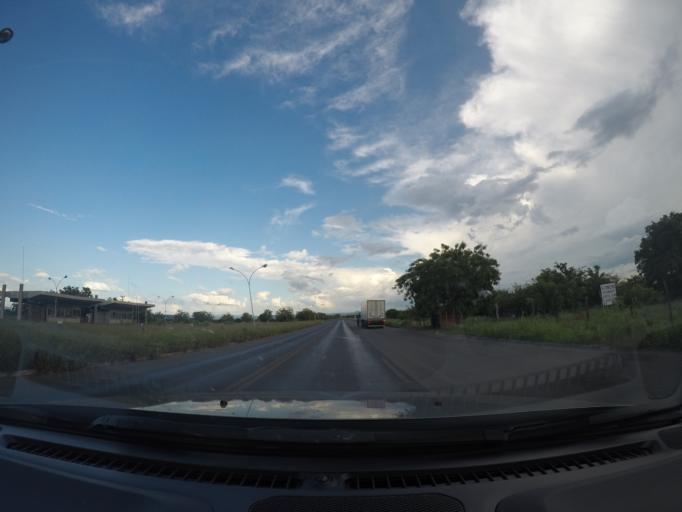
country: BR
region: Bahia
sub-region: Ibotirama
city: Ibotirama
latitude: -12.1362
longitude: -43.3300
